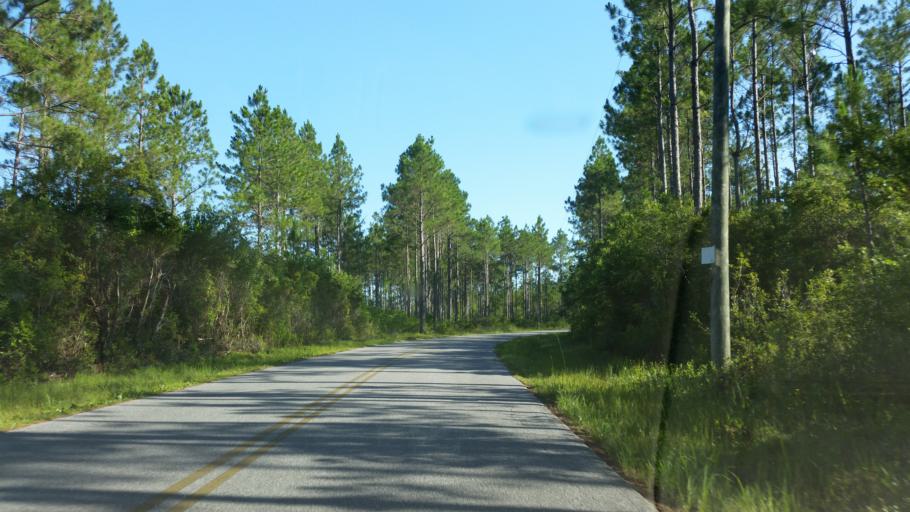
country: US
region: Florida
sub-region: Escambia County
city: Bellview
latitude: 30.4809
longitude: -87.3936
